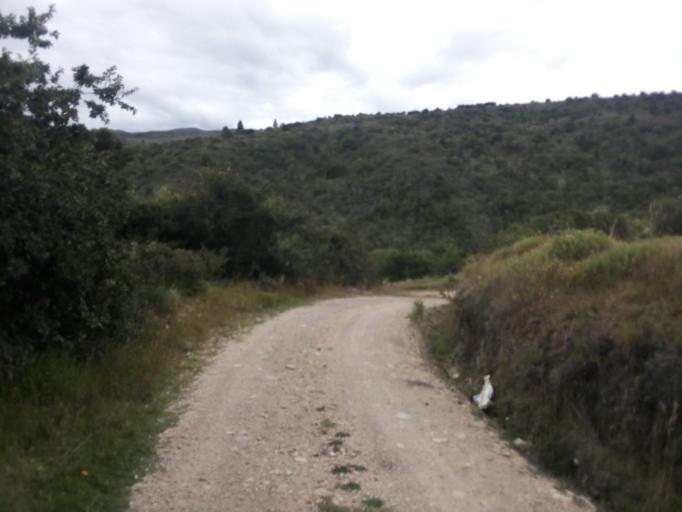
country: CO
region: Boyaca
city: Toca
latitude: 5.5863
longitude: -73.1278
